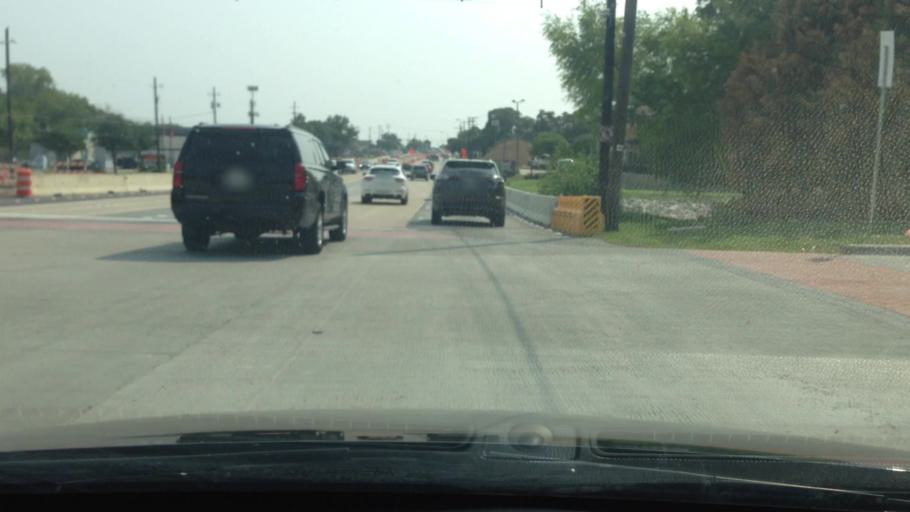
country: US
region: Texas
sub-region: Tarrant County
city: Colleyville
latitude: 32.8848
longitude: -97.1532
